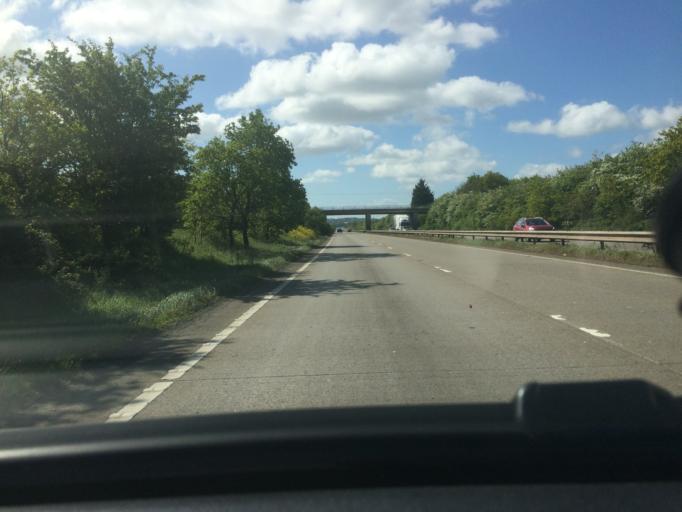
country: GB
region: Wales
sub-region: Wrexham
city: Rossett
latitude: 53.1344
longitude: -2.9464
